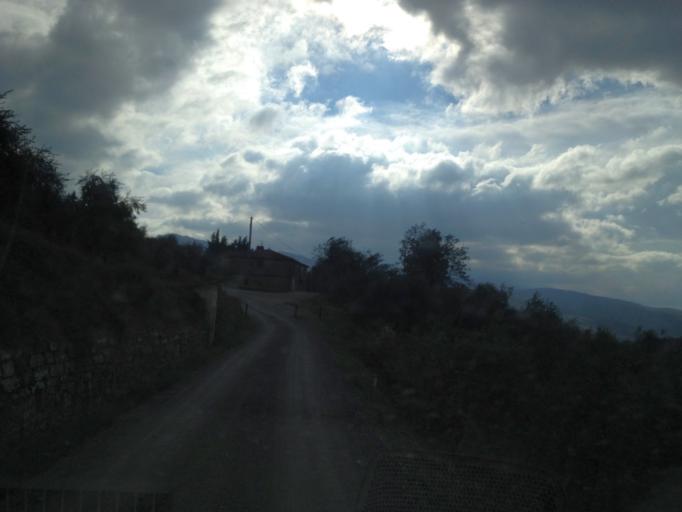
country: IT
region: Tuscany
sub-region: Province of Florence
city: Dicomano
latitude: 43.8613
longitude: 11.5050
